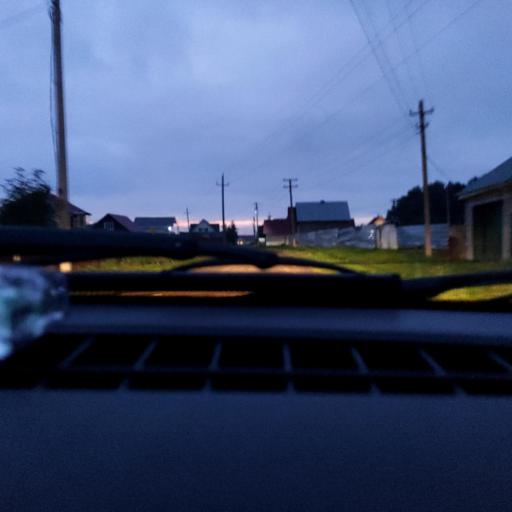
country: RU
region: Bashkortostan
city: Iglino
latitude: 54.7324
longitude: 56.3277
